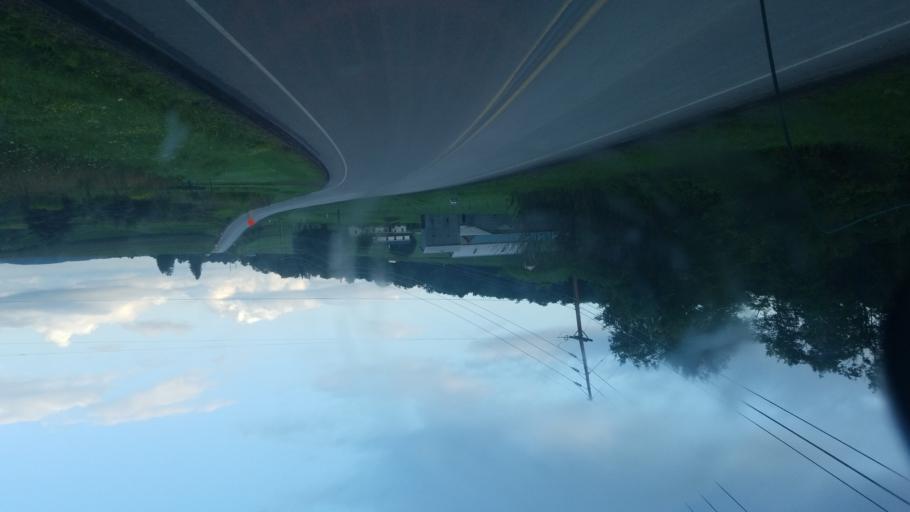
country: US
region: Pennsylvania
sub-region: Potter County
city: Galeton
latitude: 41.8561
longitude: -77.7672
